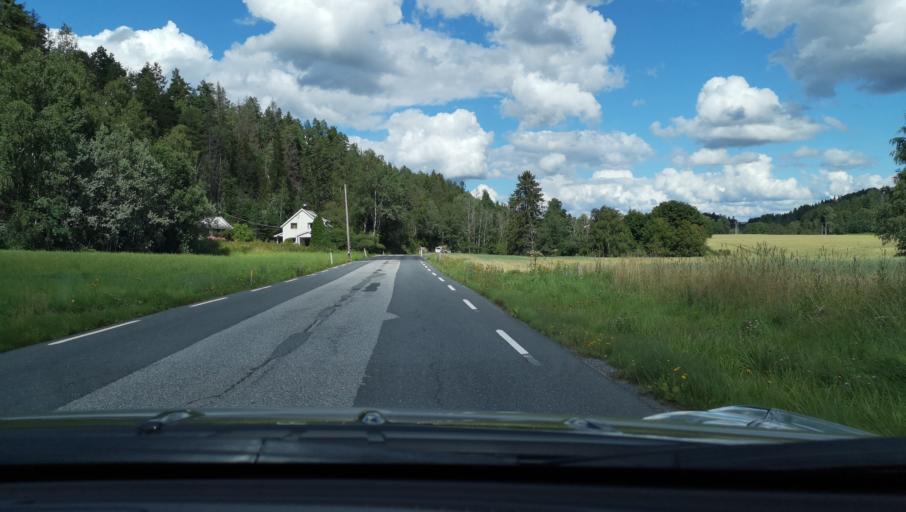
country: NO
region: Ostfold
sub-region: Hobol
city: Elvestad
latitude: 59.6329
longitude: 10.9595
